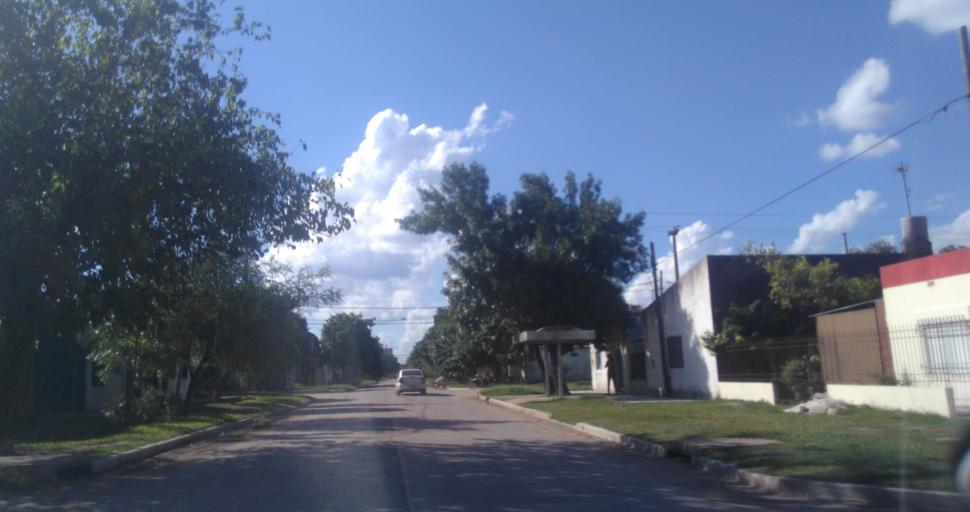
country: AR
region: Chaco
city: Resistencia
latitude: -27.4707
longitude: -58.9714
